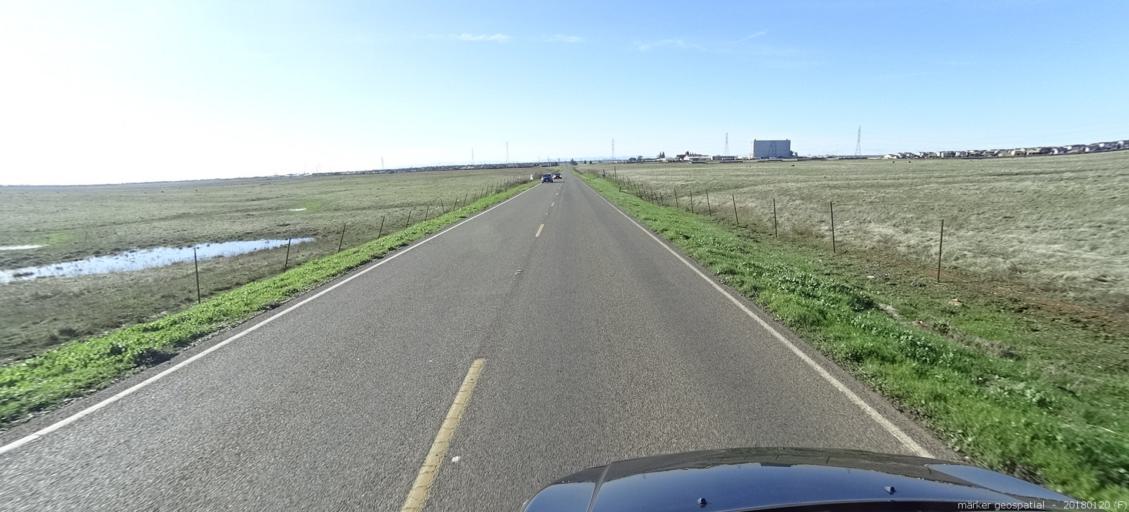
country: US
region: California
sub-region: Sacramento County
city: Gold River
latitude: 38.5592
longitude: -121.1924
